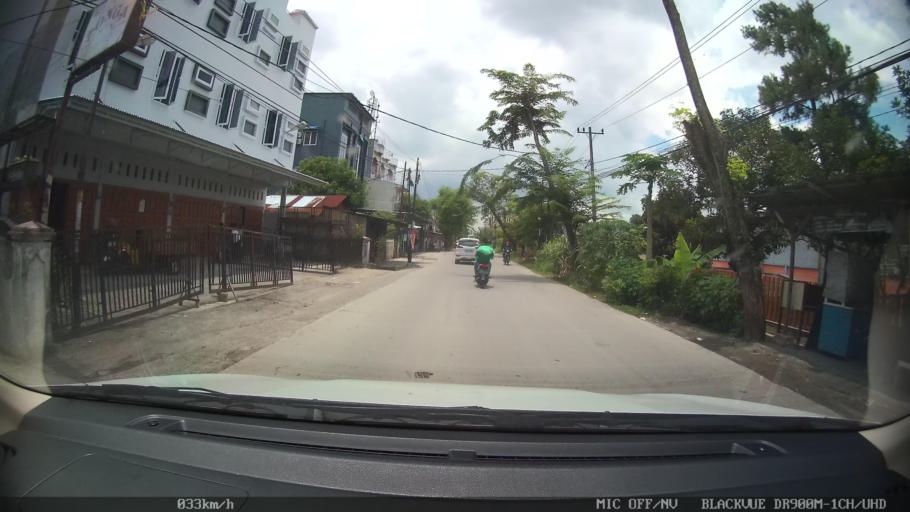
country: ID
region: North Sumatra
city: Medan
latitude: 3.6261
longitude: 98.6783
